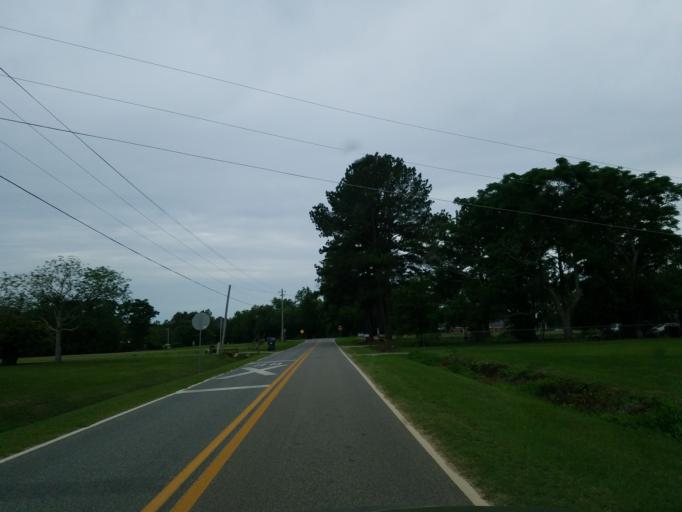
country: US
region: Georgia
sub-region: Crisp County
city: Cordele
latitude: 31.9689
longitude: -83.7002
